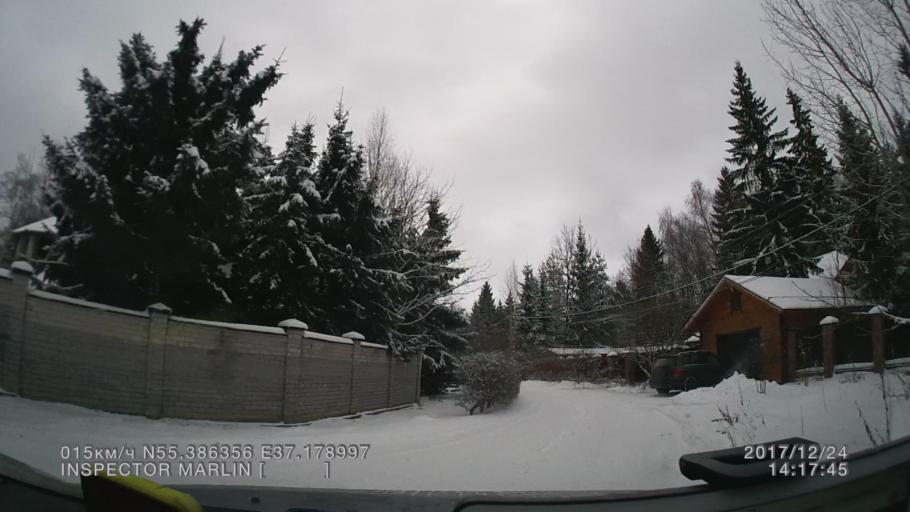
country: RU
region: Moskovskaya
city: Troitsk
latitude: 55.3863
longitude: 37.1791
